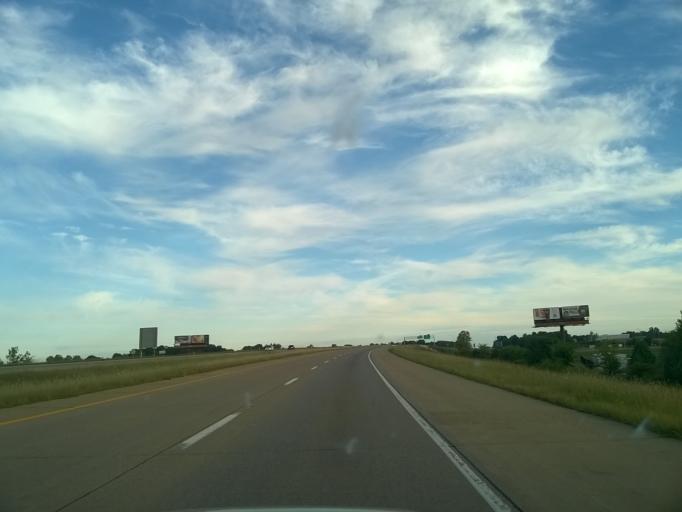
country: US
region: Indiana
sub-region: Vanderburgh County
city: Melody Hill
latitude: 37.9943
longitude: -87.4648
